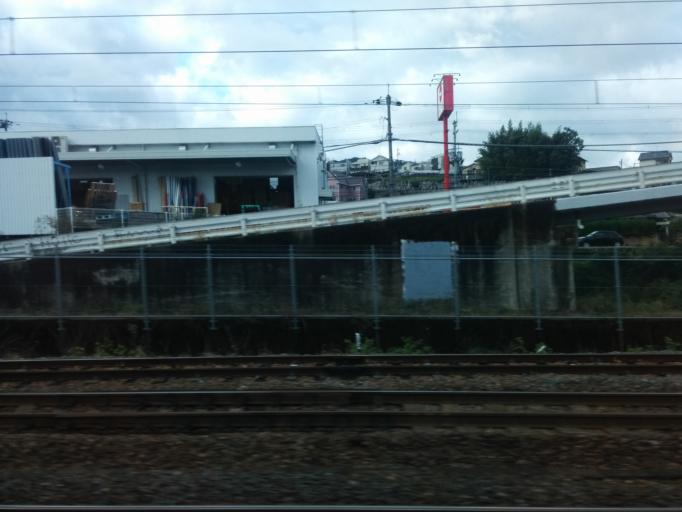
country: JP
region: Shiga Prefecture
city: Otsu-shi
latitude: 34.9964
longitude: 135.8834
